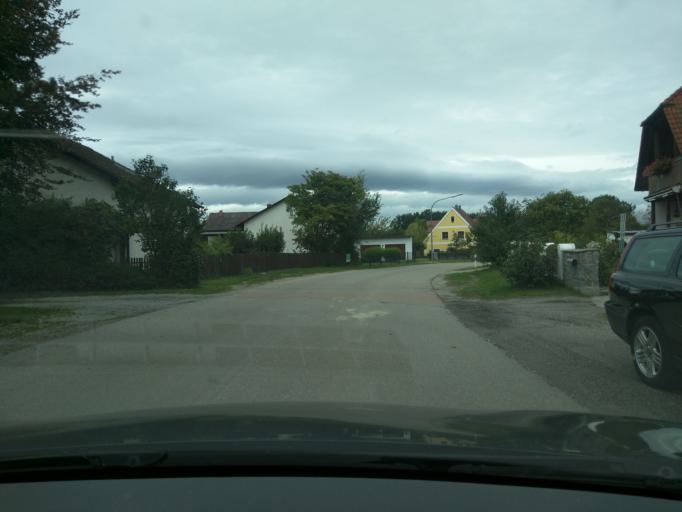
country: DE
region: Bavaria
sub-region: Upper Palatinate
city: Schwarzenfeld
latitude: 49.3596
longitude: 12.1490
